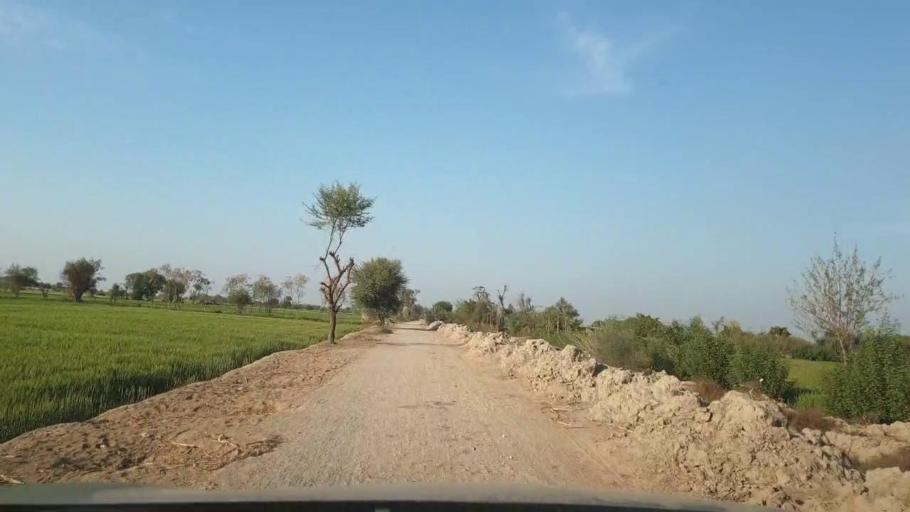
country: PK
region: Sindh
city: Tando Adam
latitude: 25.6943
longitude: 68.7023
